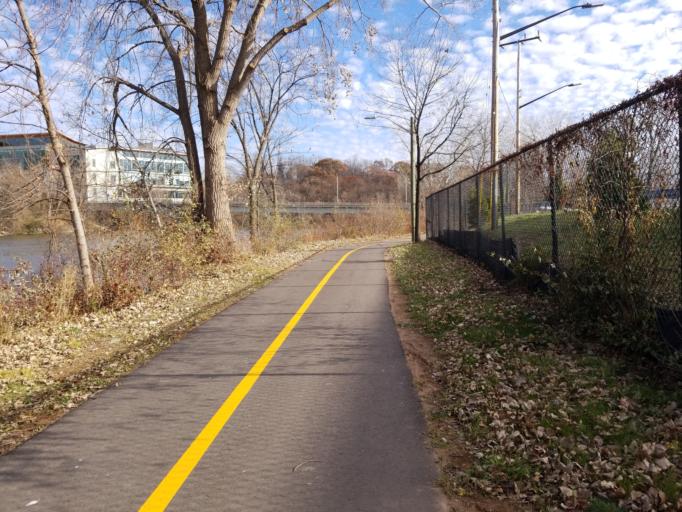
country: US
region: Wisconsin
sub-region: Outagamie County
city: Appleton
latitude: 44.2585
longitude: -88.3990
